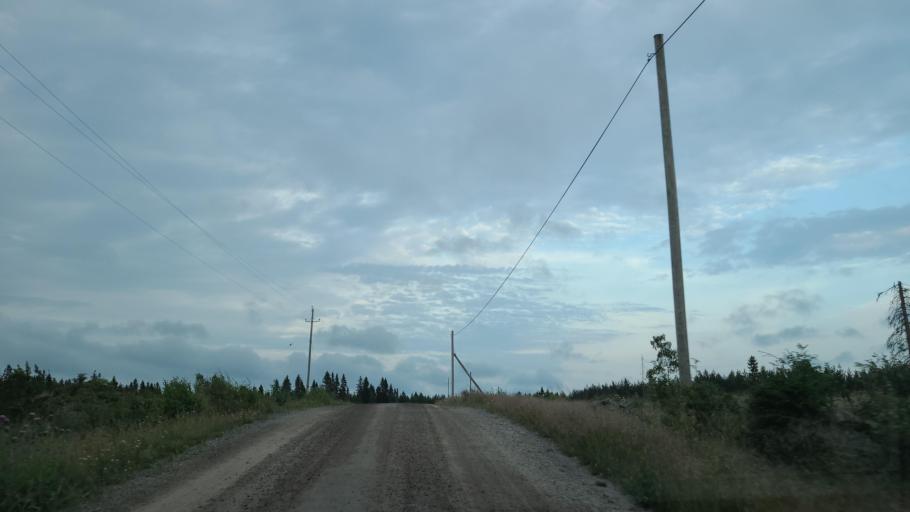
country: FI
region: Ostrobothnia
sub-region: Vaasa
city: Replot
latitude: 63.3182
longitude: 21.1509
